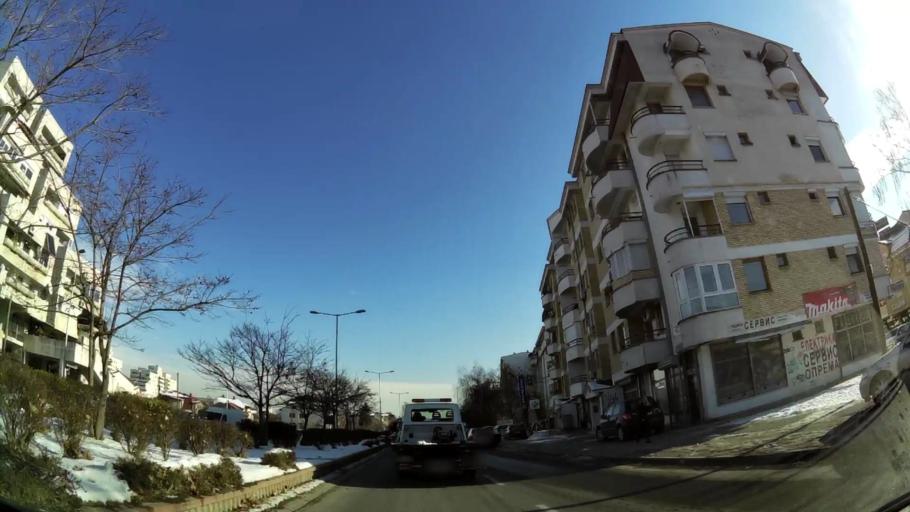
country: MK
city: Krushopek
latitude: 42.0067
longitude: 21.3677
